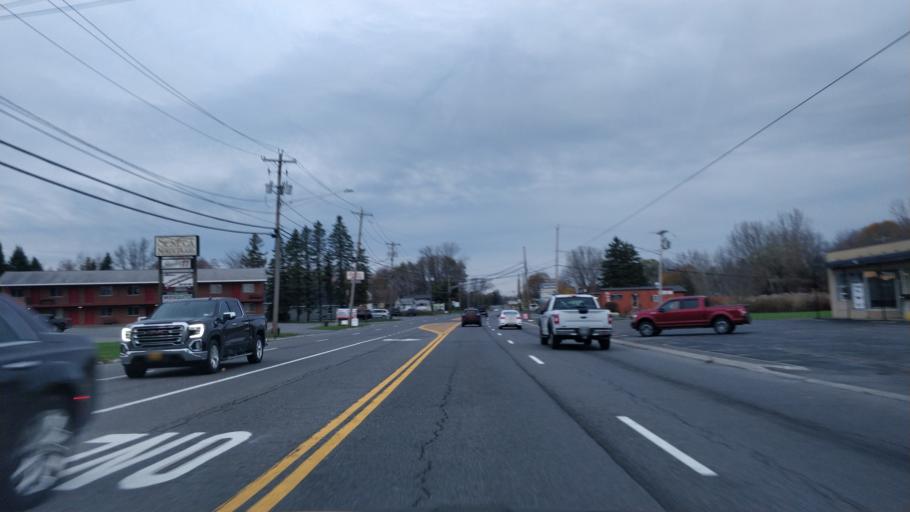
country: US
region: New York
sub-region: Onondaga County
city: North Syracuse
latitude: 43.1638
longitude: -76.1194
